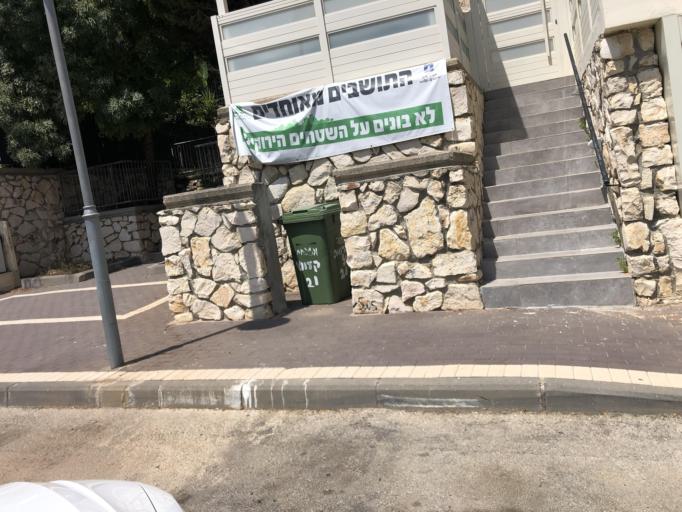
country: IL
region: Haifa
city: Daliyat el Karmil
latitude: 32.6351
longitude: 35.0868
